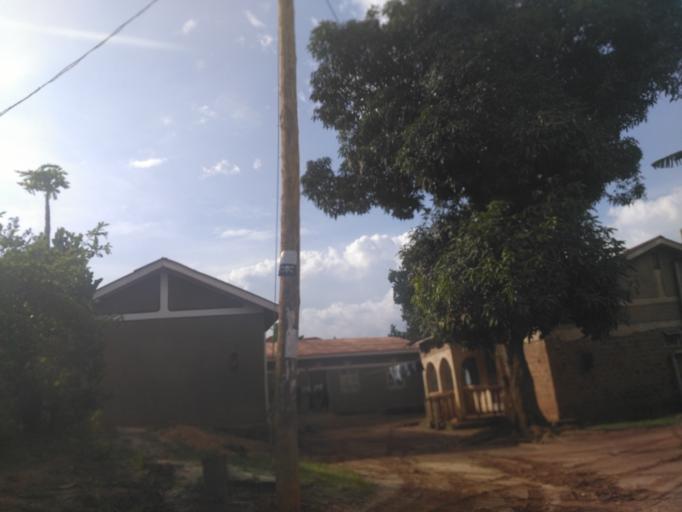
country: UG
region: Central Region
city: Kampala Central Division
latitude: 0.3597
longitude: 32.5852
